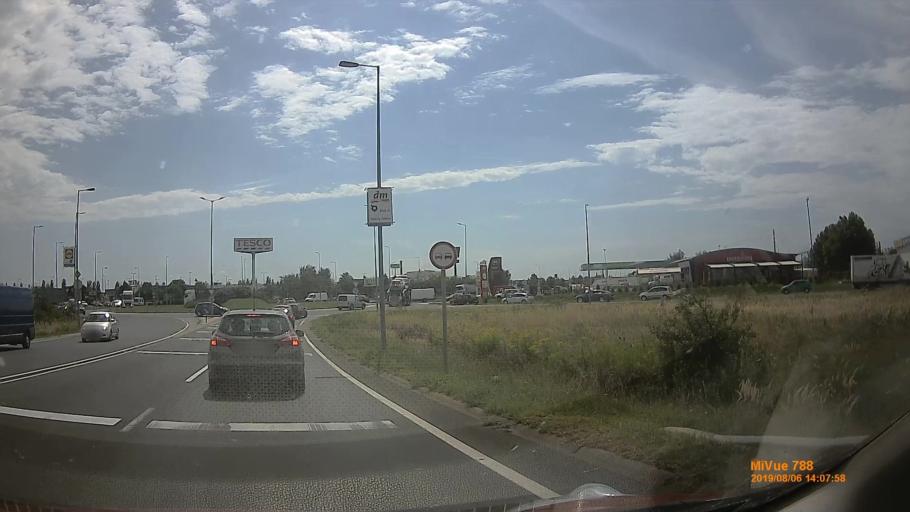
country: HU
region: Vas
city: Szombathely
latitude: 47.2434
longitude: 16.6540
